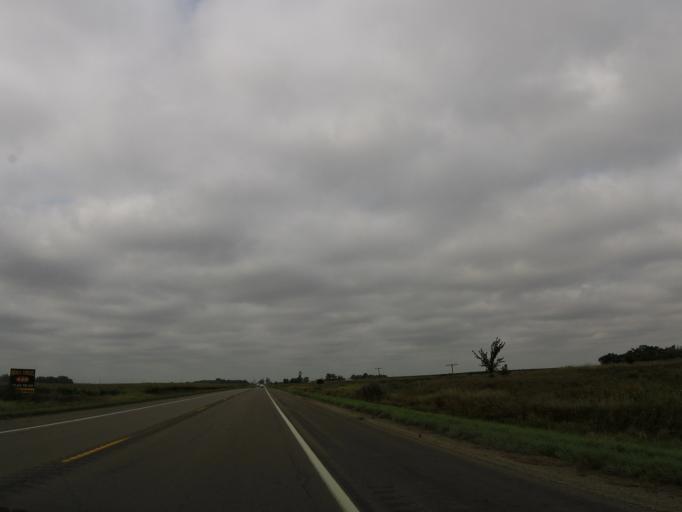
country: US
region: Minnesota
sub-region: Renville County
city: Olivia
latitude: 44.7837
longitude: -95.0427
